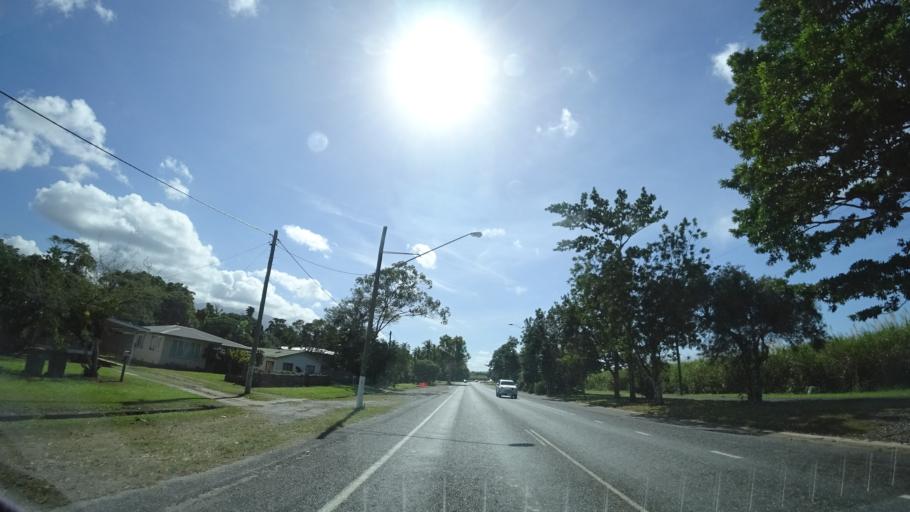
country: AU
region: Queensland
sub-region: Cairns
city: Port Douglas
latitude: -16.4721
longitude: 145.3738
